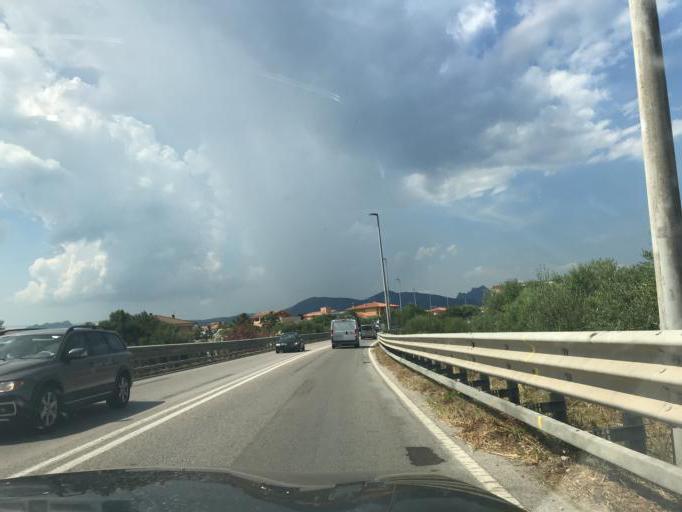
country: IT
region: Sardinia
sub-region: Provincia di Olbia-Tempio
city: Olbia
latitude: 40.9123
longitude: 9.5026
